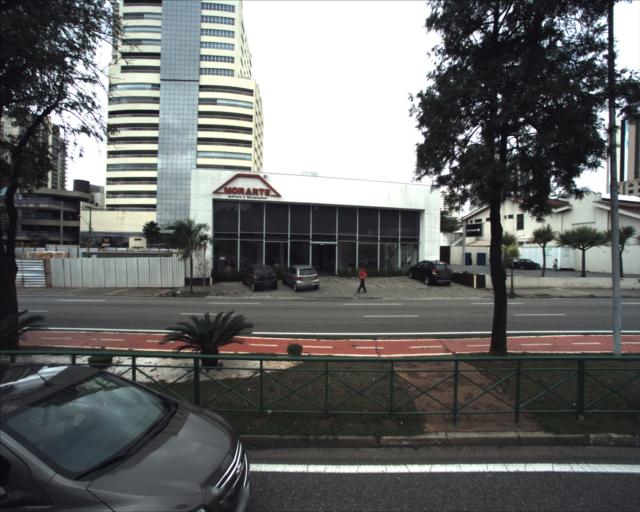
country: BR
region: Sao Paulo
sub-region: Sorocaba
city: Sorocaba
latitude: -23.5195
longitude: -47.4645
